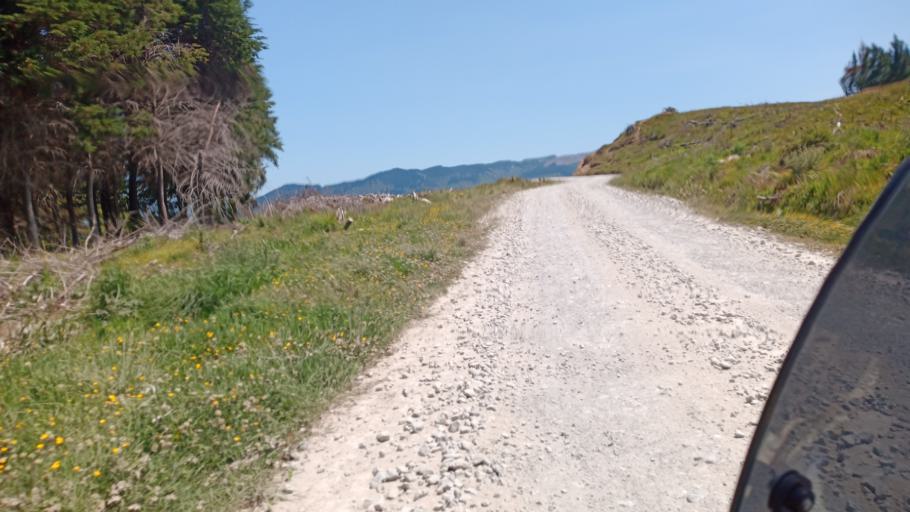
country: NZ
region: Gisborne
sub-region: Gisborne District
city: Gisborne
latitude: -38.2915
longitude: 178.0180
